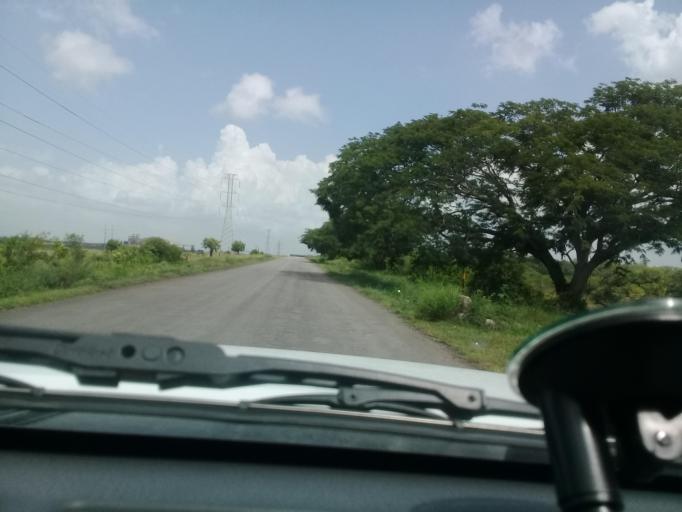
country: MX
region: Veracruz
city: Moralillo
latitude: 22.2266
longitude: -98.0127
